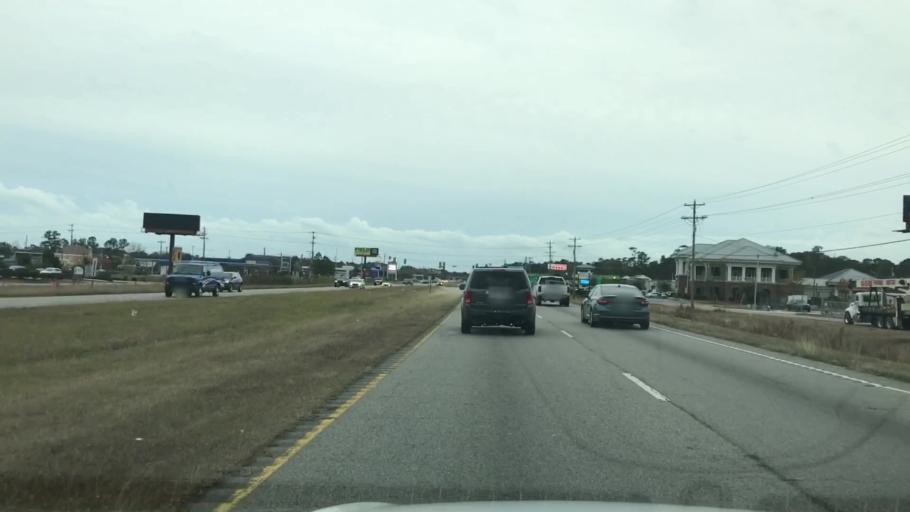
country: US
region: South Carolina
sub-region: Horry County
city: Garden City
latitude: 33.5872
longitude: -79.0271
